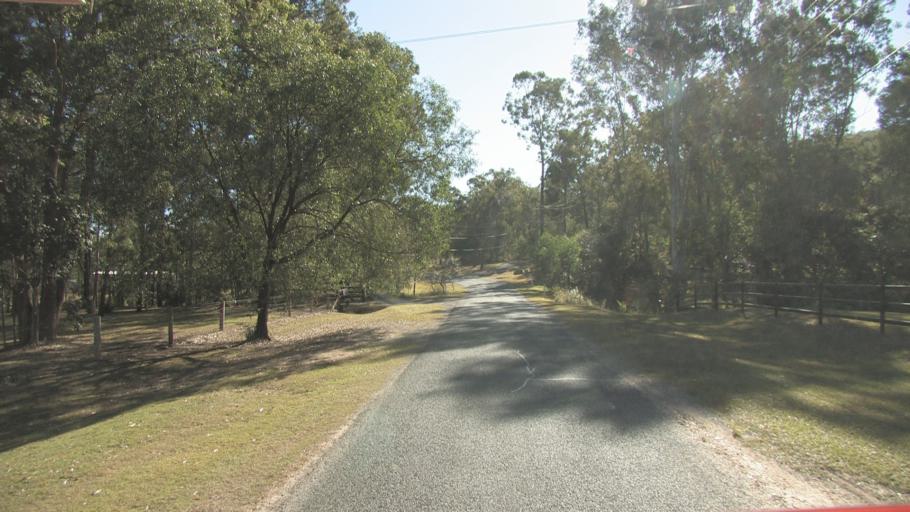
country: AU
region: Queensland
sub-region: Logan
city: Windaroo
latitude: -27.7918
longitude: 153.1469
